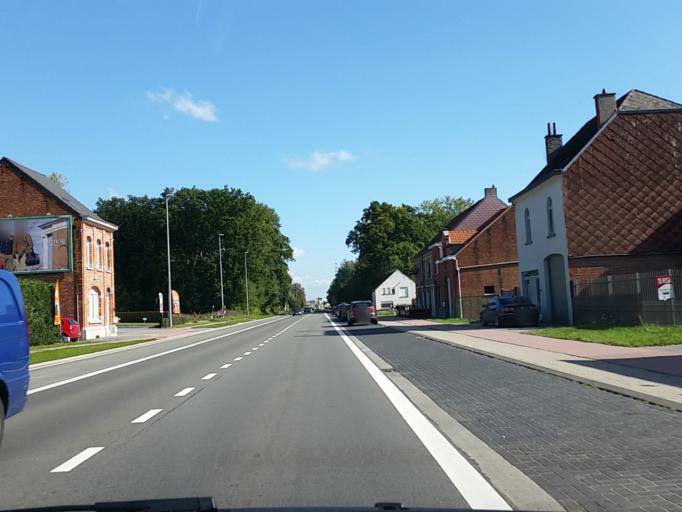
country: BE
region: Flanders
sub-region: Provincie Vlaams-Brabant
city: Boortmeerbeek
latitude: 50.9511
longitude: 4.5843
